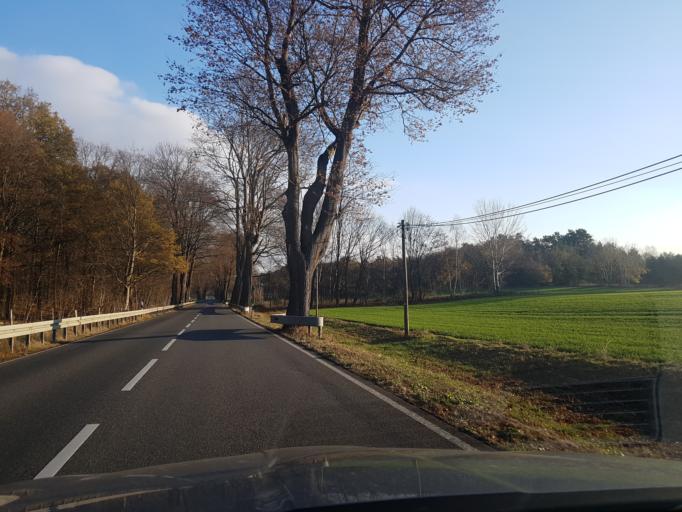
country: DE
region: Brandenburg
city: Drahnsdorf
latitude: 51.8240
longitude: 13.6135
